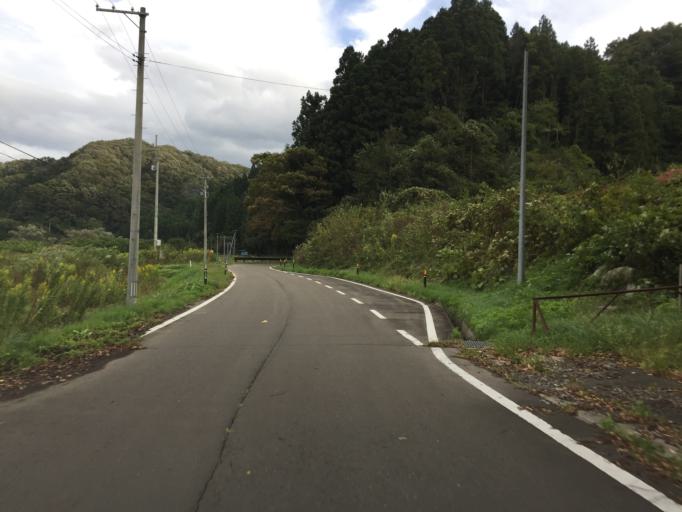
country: JP
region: Miyagi
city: Marumori
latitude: 37.9275
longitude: 140.7362
